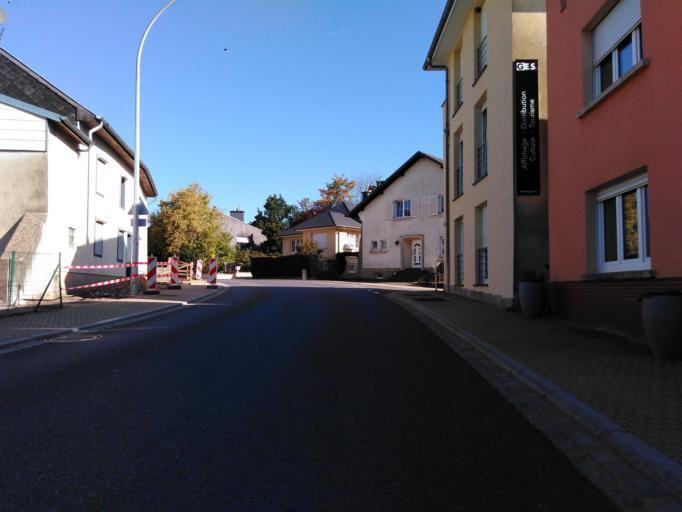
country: LU
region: Luxembourg
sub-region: Canton de Capellen
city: Steinfort
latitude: 49.6564
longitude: 5.9148
